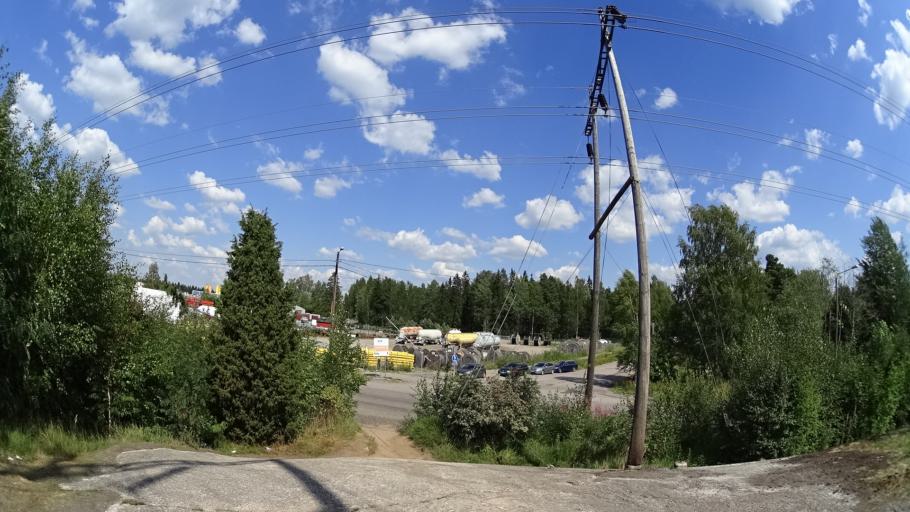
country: FI
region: Uusimaa
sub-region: Helsinki
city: Vantaa
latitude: 60.3399
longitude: 24.9947
